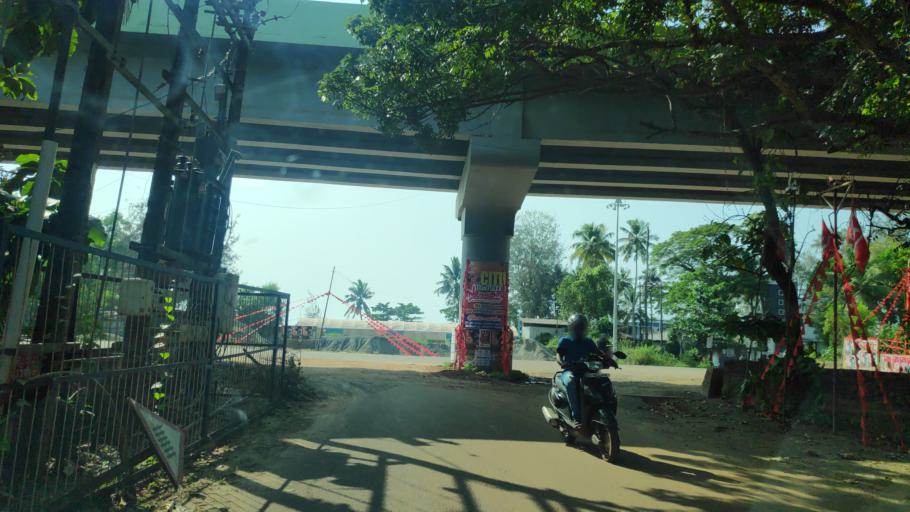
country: IN
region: Kerala
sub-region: Alappuzha
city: Alleppey
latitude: 9.4973
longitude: 76.3181
